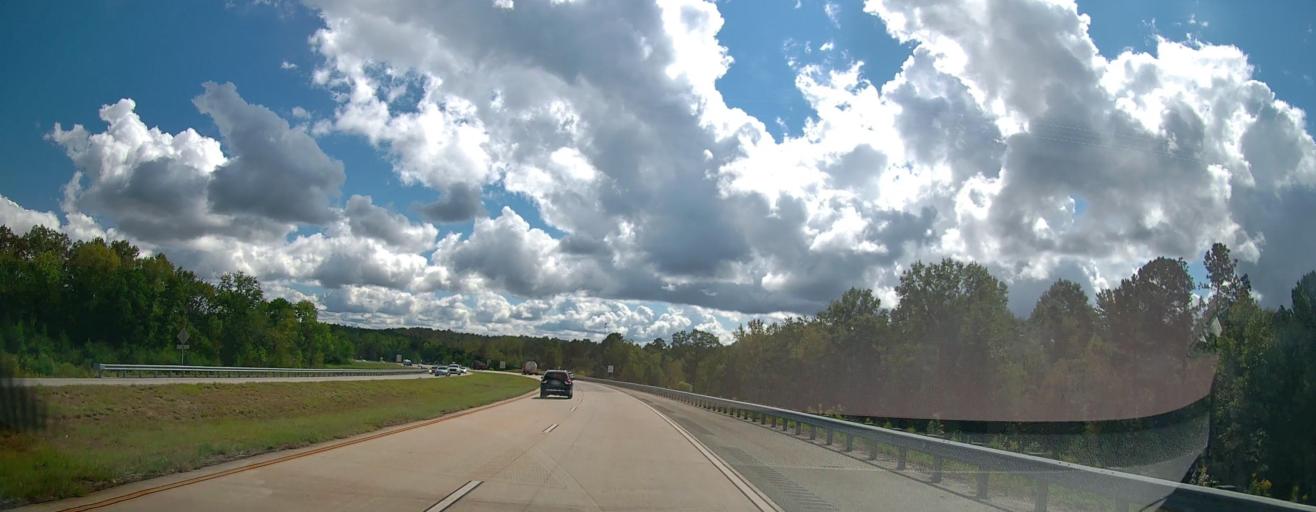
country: US
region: Georgia
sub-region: Jones County
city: Gray
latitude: 32.9950
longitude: -83.5742
